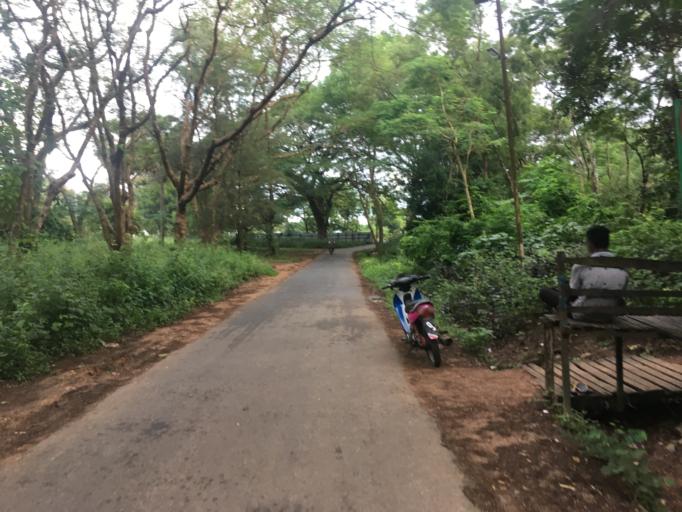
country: MM
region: Mon
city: Mawlamyine
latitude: 16.4695
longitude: 97.6279
